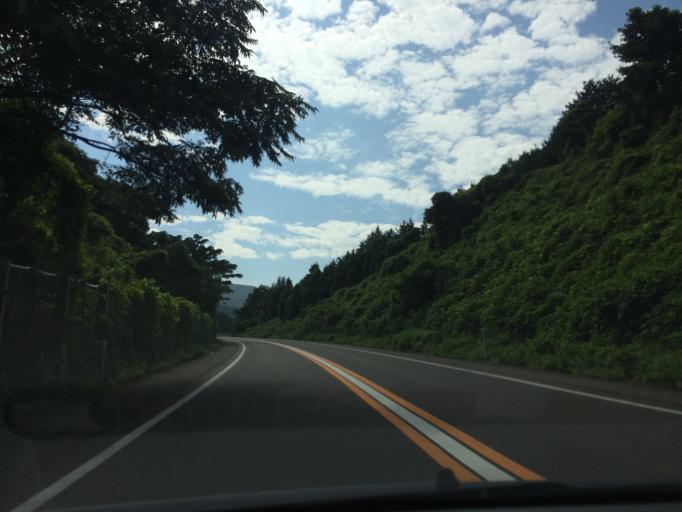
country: JP
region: Tottori
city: Kurayoshi
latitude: 35.3425
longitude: 133.7489
